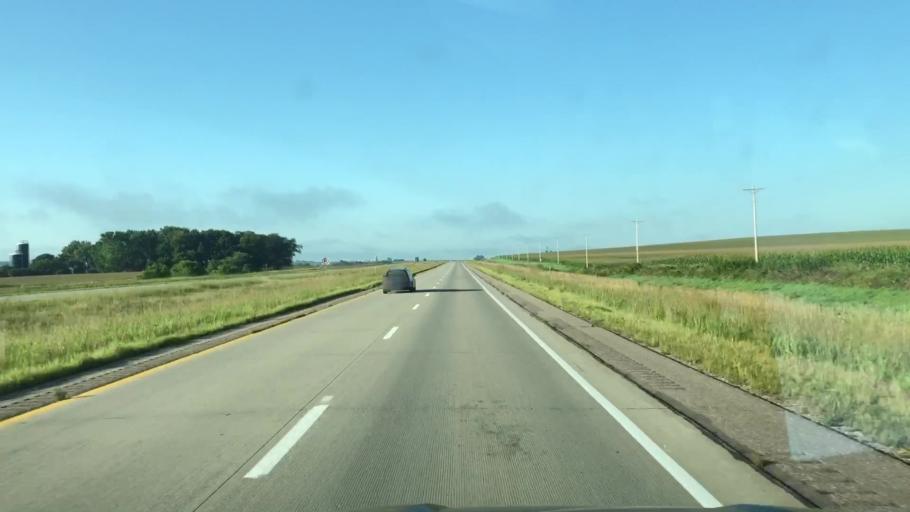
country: US
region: Iowa
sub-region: Sioux County
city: Alton
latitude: 42.9469
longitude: -96.0390
